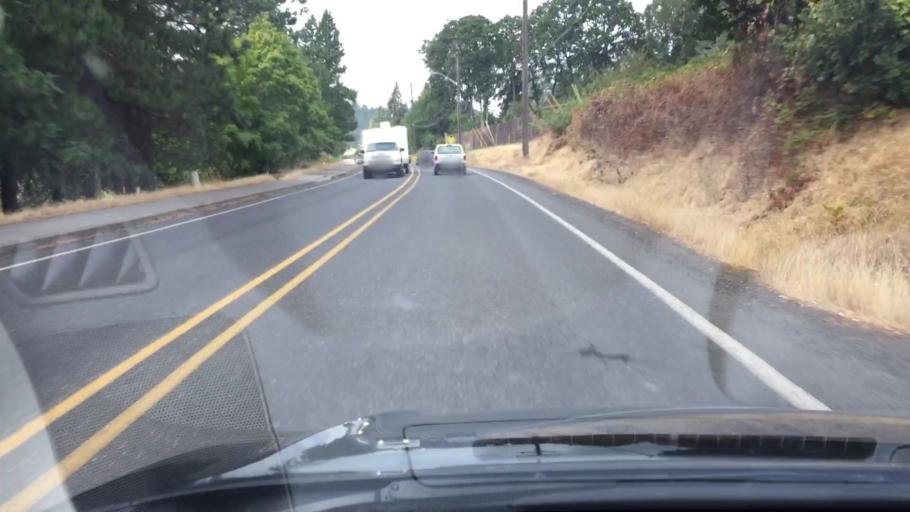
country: US
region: Washington
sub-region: Klickitat County
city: White Salmon
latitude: 45.7236
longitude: -121.4755
